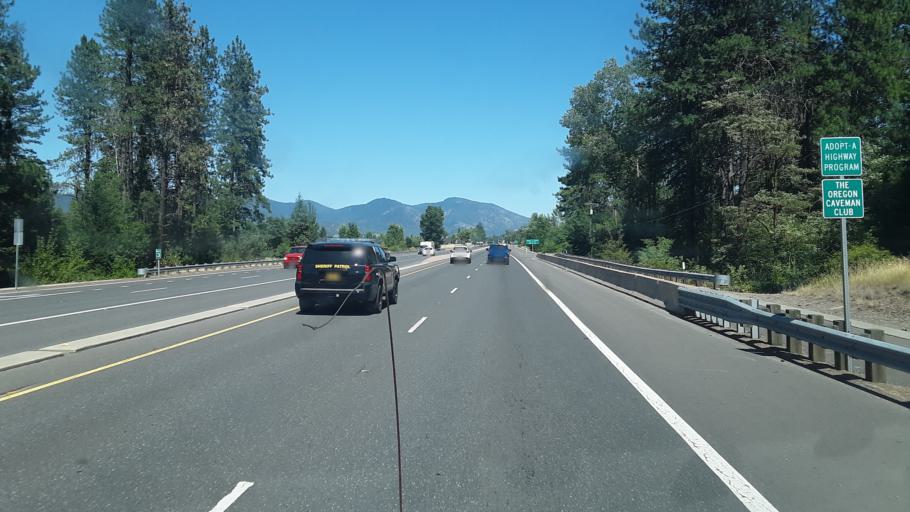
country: US
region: Oregon
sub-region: Josephine County
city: Redwood
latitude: 42.4159
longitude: -123.3855
